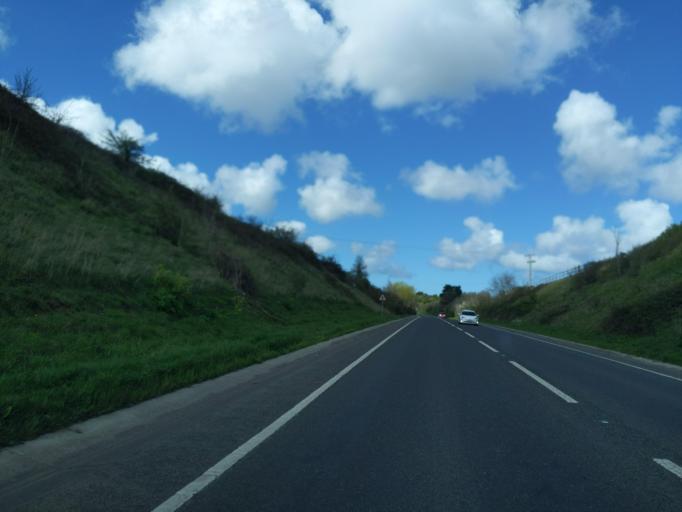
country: GB
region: England
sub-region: Cornwall
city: Wadebridge
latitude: 50.5179
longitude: -4.8195
